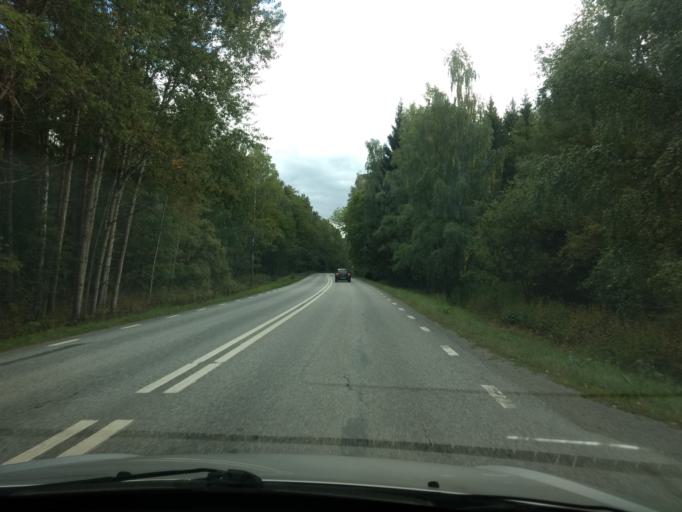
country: SE
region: Uppsala
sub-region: Uppsala Kommun
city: Saevja
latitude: 59.7508
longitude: 17.6522
